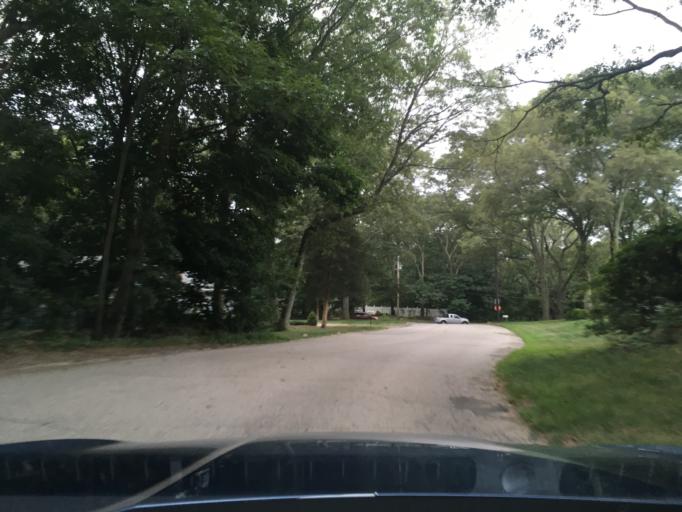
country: US
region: Rhode Island
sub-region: Kent County
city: East Greenwich
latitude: 41.6471
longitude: -71.4859
